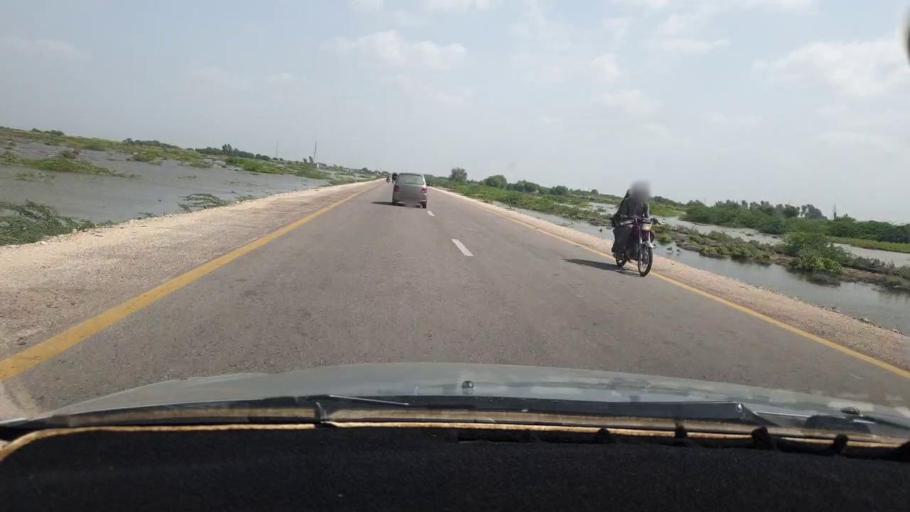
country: PK
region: Sindh
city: Digri
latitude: 25.1241
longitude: 69.1466
